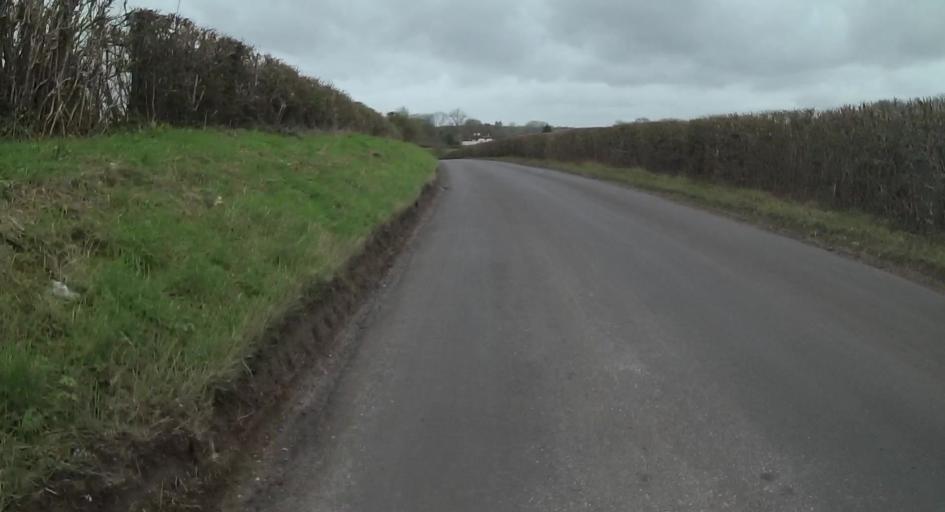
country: GB
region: England
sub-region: Hampshire
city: Kingsclere
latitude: 51.3288
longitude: -1.2747
